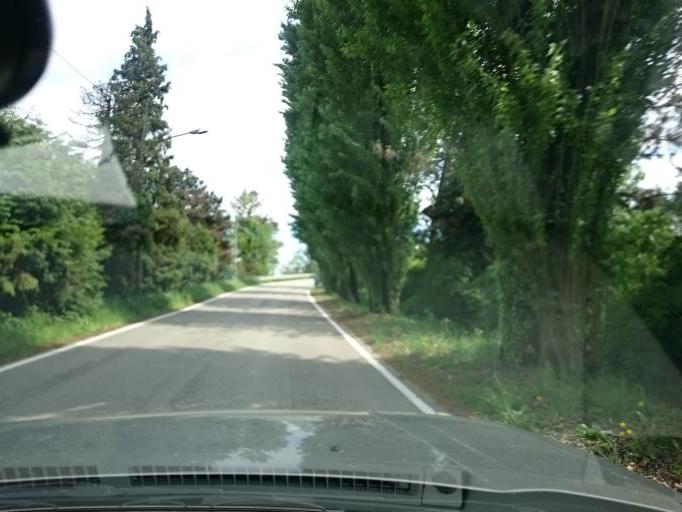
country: IT
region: Veneto
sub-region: Provincia di Vicenza
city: Torri di Quartesolo
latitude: 45.5176
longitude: 11.5847
